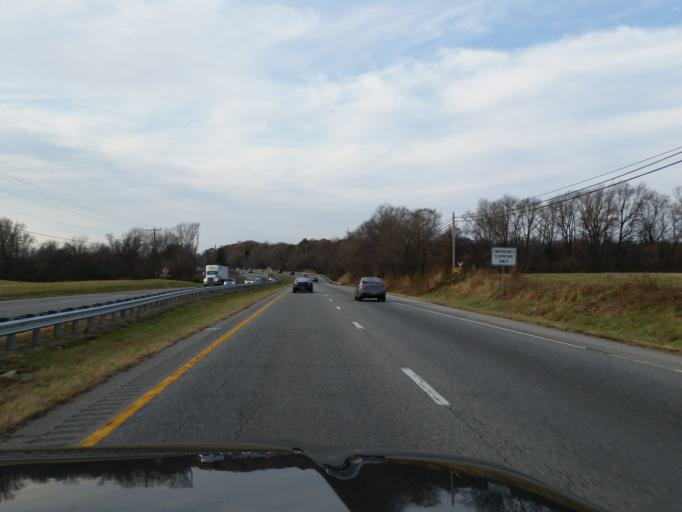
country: US
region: Maryland
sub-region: Queen Anne's County
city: Grasonville
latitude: 38.9733
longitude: -76.1248
